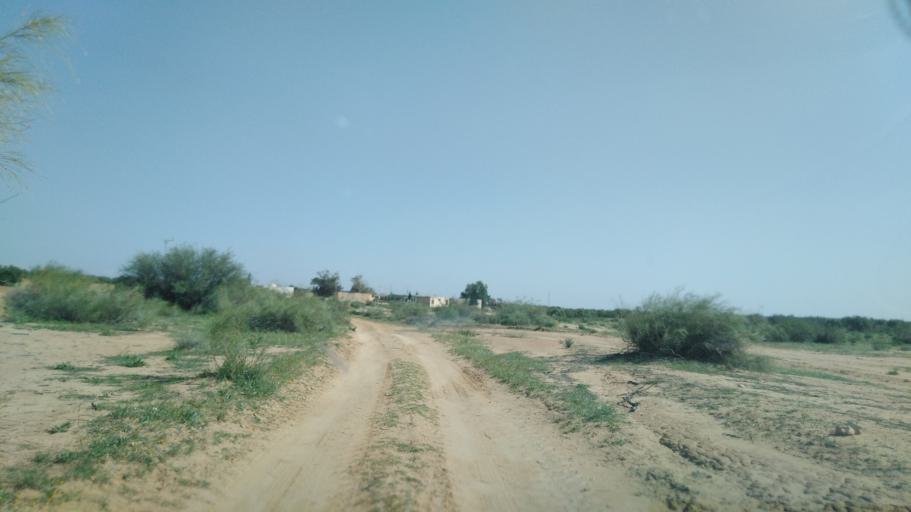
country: TN
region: Safaqis
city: Bi'r `Ali Bin Khalifah
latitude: 34.7797
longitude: 10.3644
